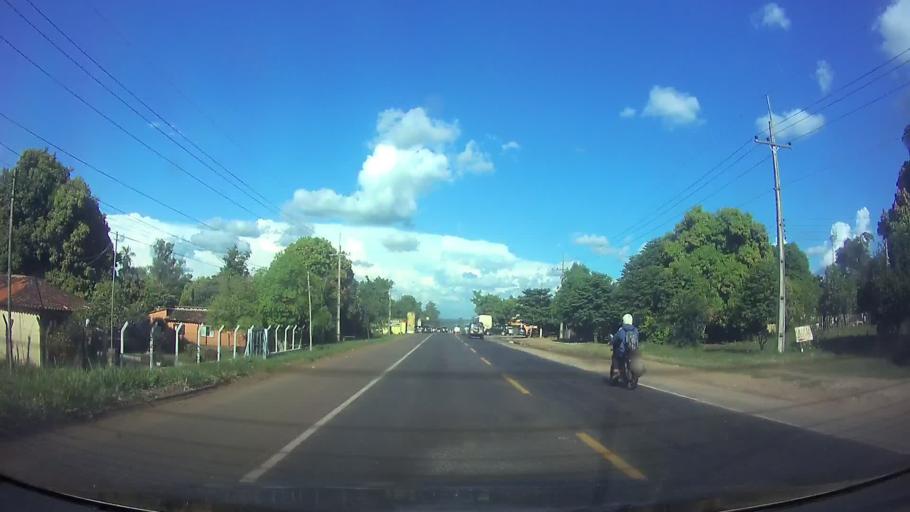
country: PY
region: Cordillera
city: Eusebio Ayala
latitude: -25.3818
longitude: -57.0026
